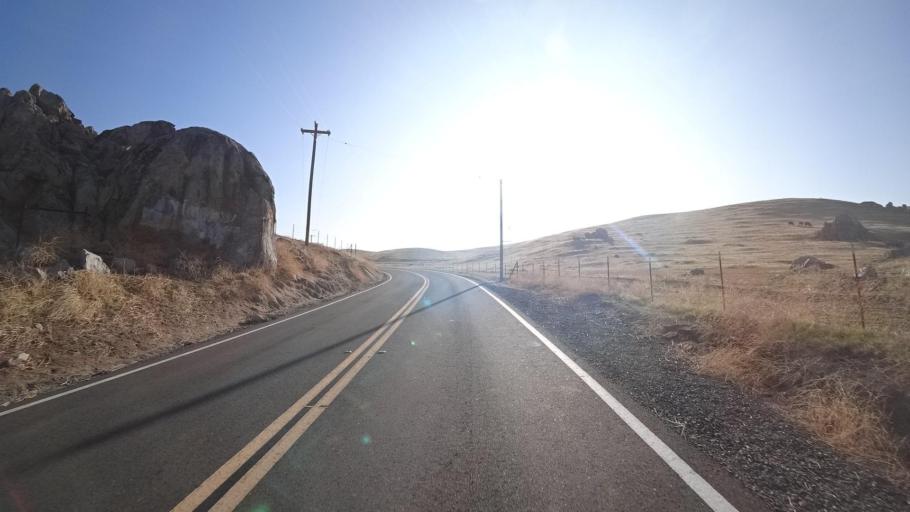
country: US
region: California
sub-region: Tulare County
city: Richgrove
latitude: 35.7428
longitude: -118.8997
